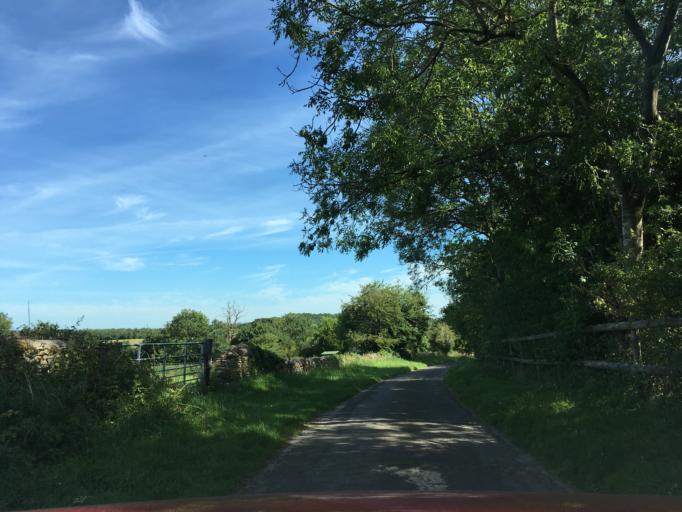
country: GB
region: England
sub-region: Wiltshire
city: Nettleton
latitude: 51.4859
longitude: -2.2660
